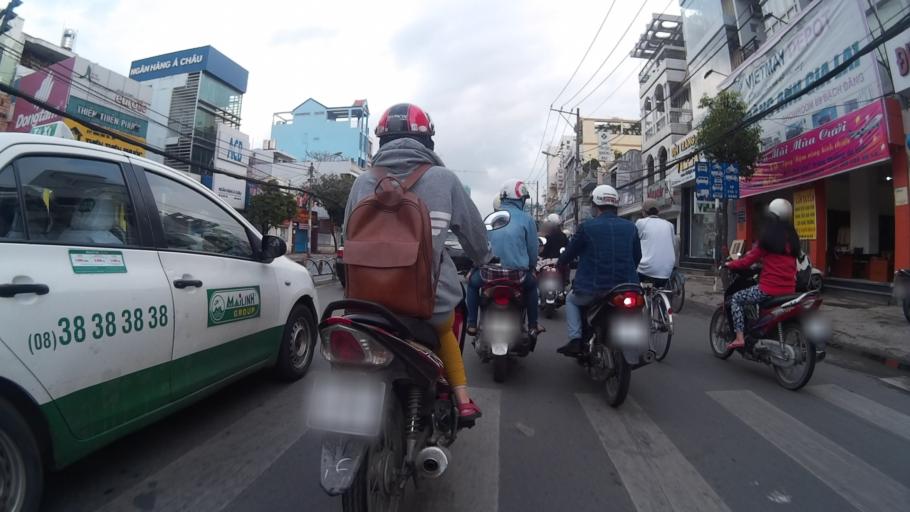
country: VN
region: Ho Chi Minh City
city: Quan Binh Thanh
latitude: 10.8029
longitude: 106.7094
